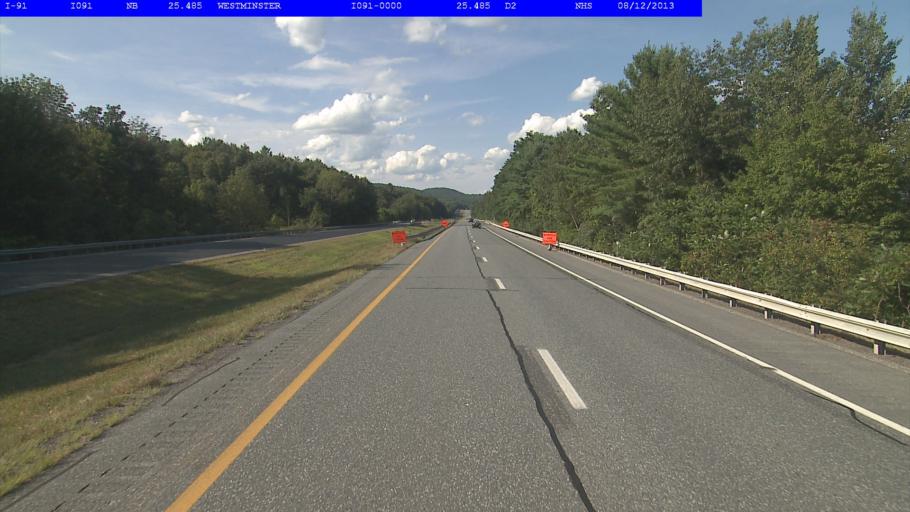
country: US
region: Vermont
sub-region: Windham County
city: Bellows Falls
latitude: 43.0479
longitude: -72.4702
